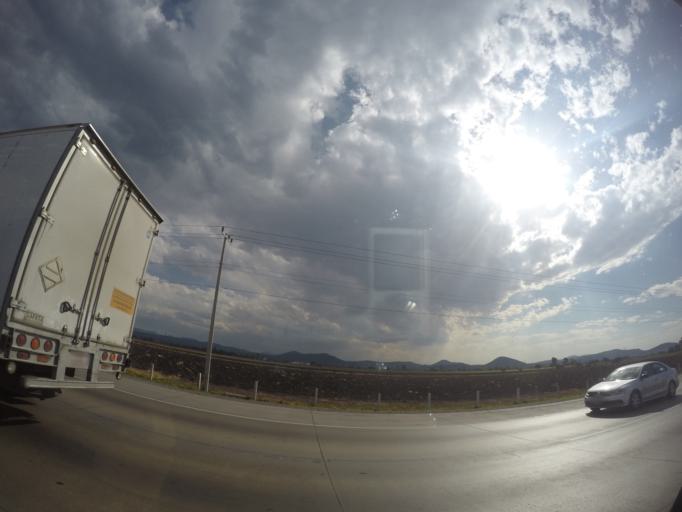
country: MX
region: Queretaro
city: El Sauz
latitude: 20.4625
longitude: -100.0981
